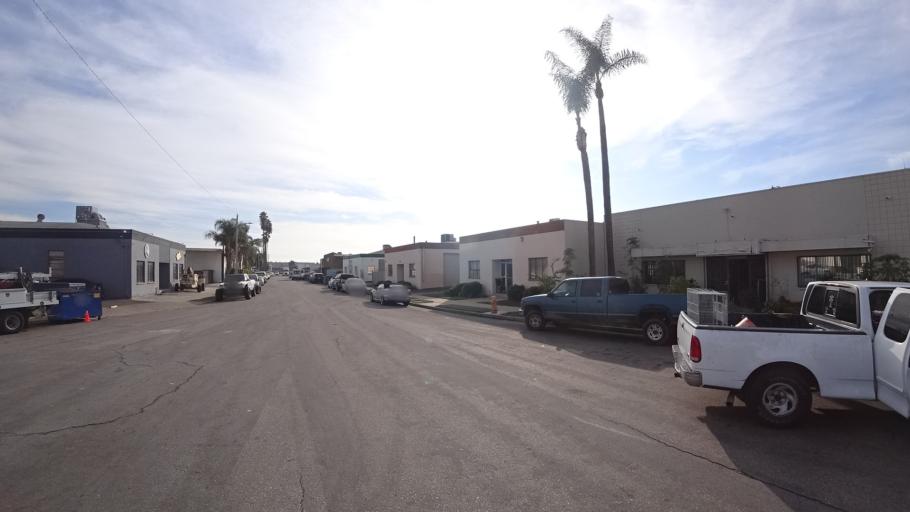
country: US
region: California
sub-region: Orange County
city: Garden Grove
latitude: 33.7625
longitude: -117.9239
